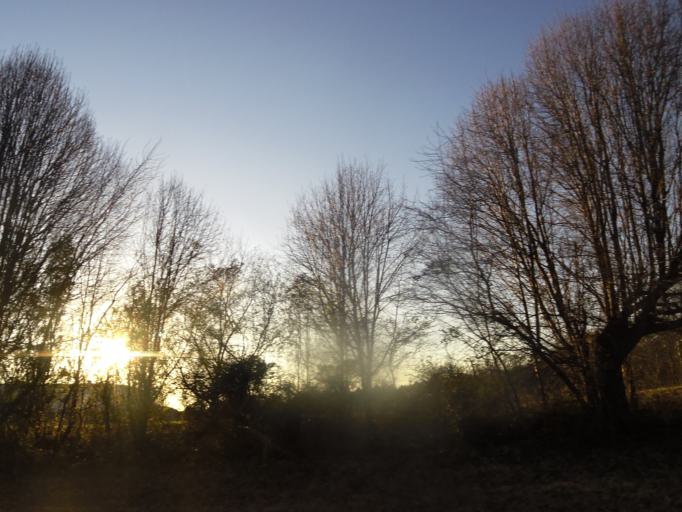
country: US
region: Virginia
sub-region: City of Petersburg
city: Petersburg
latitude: 37.1968
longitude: -77.4274
